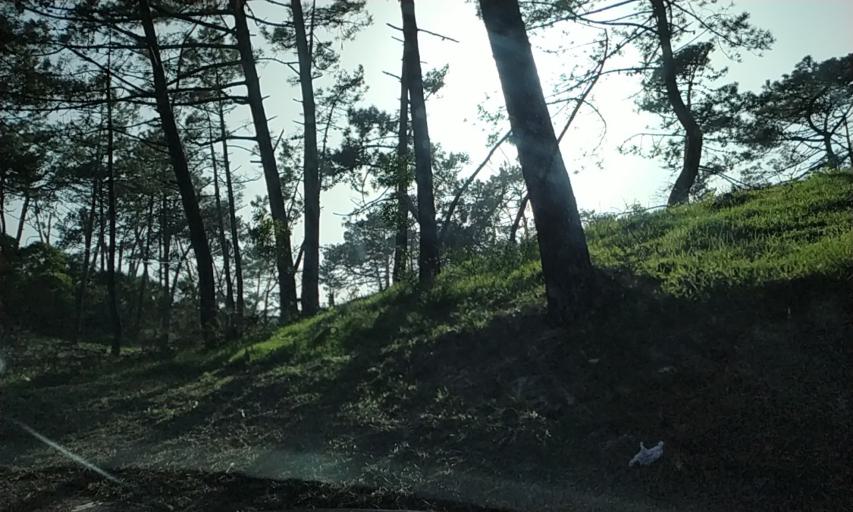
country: PT
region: Leiria
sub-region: Alcobaca
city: Pataias
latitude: 39.7580
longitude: -9.0264
